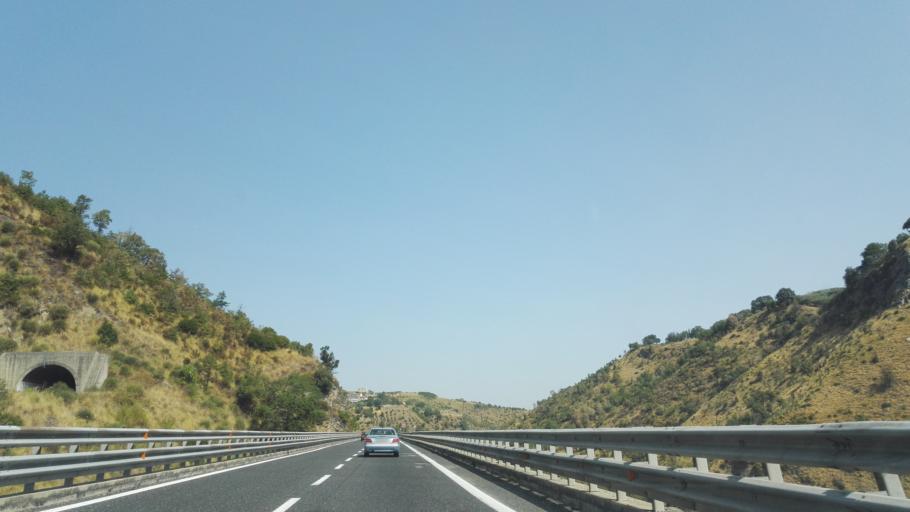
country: IT
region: Calabria
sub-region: Provincia di Cosenza
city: Laurignano
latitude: 39.2627
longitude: 16.2513
